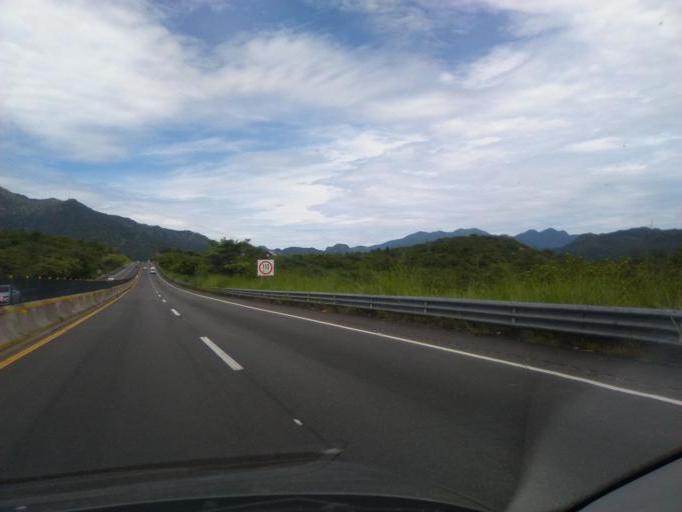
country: MX
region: Guerrero
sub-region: Chilpancingo de los Bravo
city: Cajelitos
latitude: 17.2698
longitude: -99.5113
